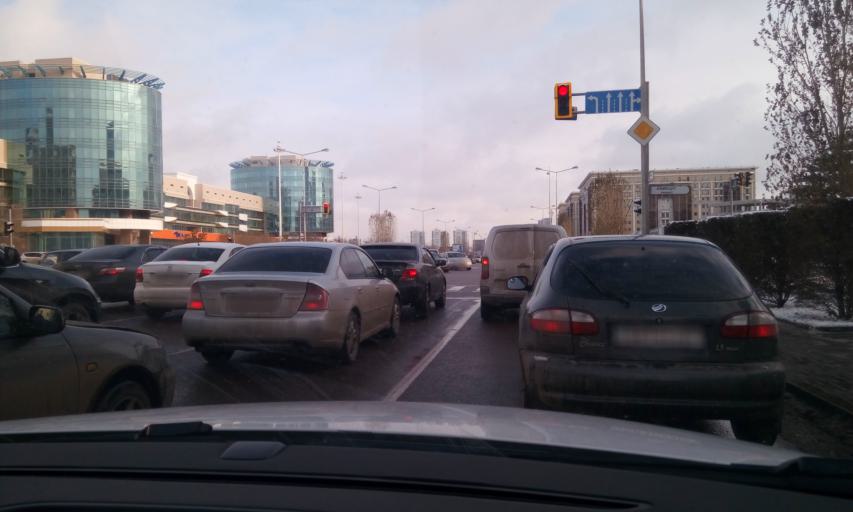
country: KZ
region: Astana Qalasy
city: Astana
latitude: 51.1340
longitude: 71.4301
